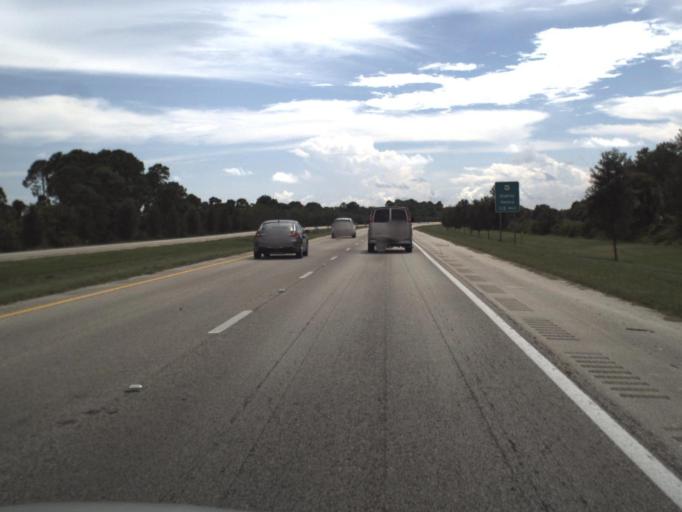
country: US
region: Florida
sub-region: Sarasota County
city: Laurel
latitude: 27.1604
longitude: -82.4589
